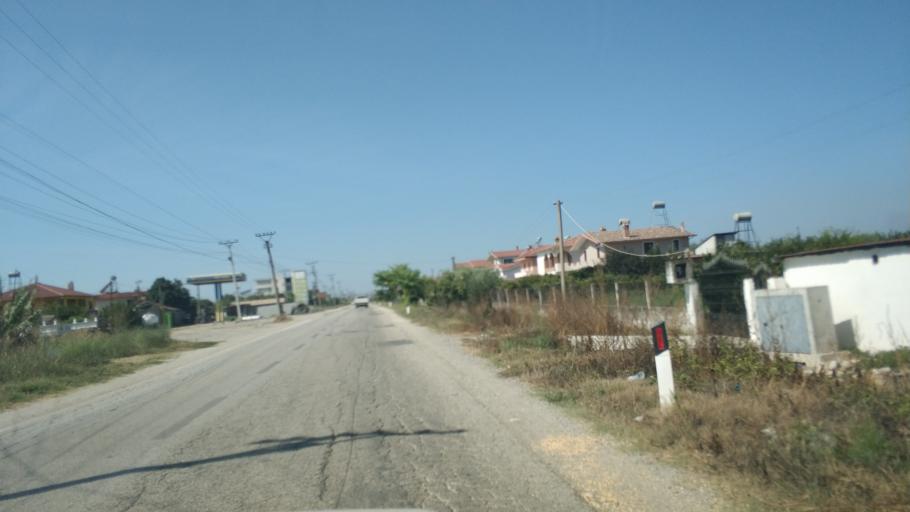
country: AL
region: Fier
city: Terbuf
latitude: 41.0519
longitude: 19.6429
